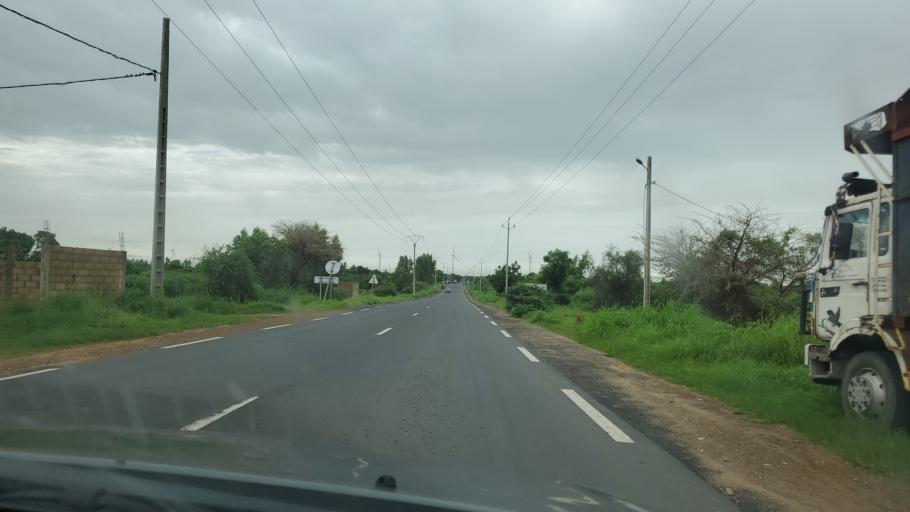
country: SN
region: Thies
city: Kayar
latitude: 15.0993
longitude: -16.9129
